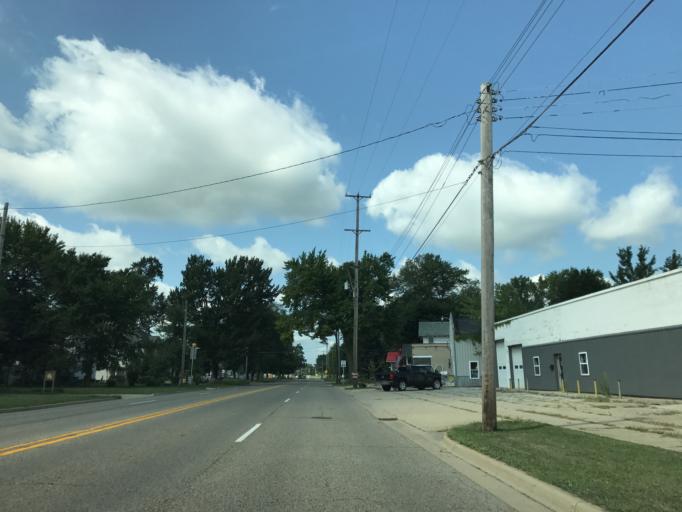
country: US
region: Michigan
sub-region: Branch County
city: Bronson
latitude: 41.8716
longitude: -85.1997
